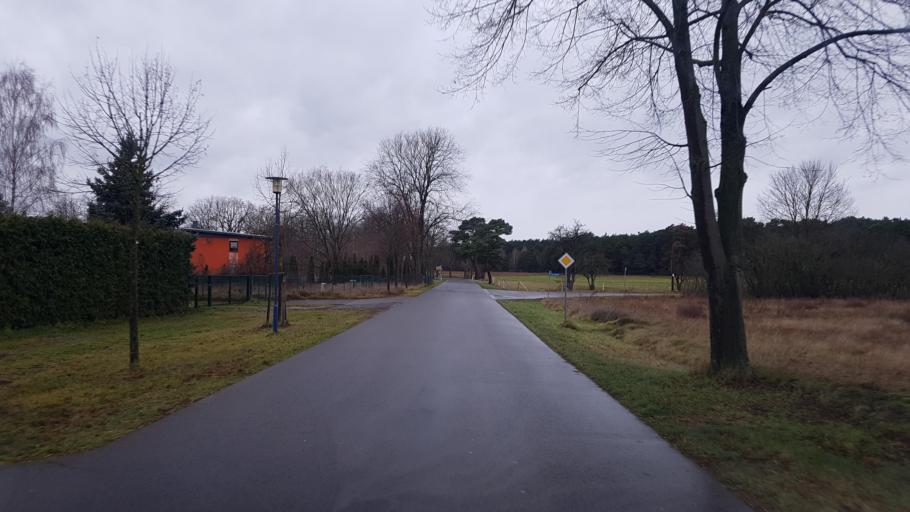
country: DE
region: Brandenburg
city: Tauche
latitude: 52.1083
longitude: 14.1109
